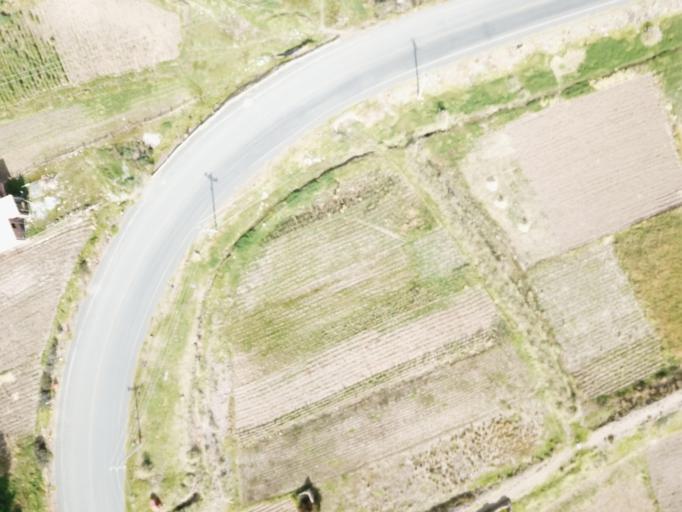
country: BO
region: La Paz
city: Achacachi
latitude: -16.0525
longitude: -68.8170
